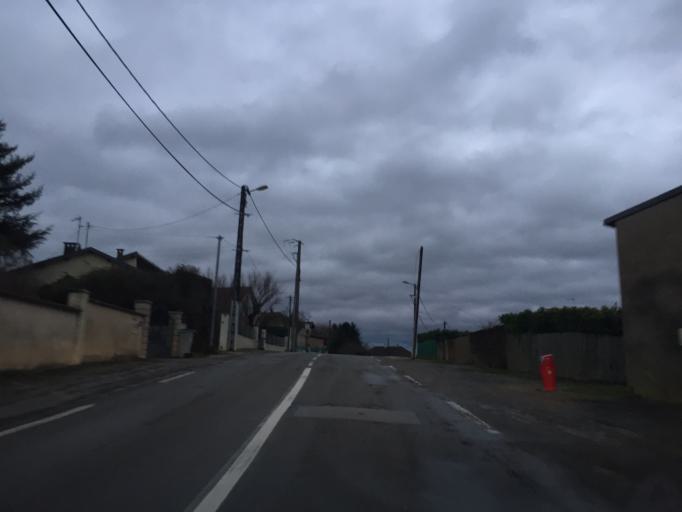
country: FR
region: Franche-Comte
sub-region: Departement du Jura
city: Dole
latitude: 47.1090
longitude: 5.4773
